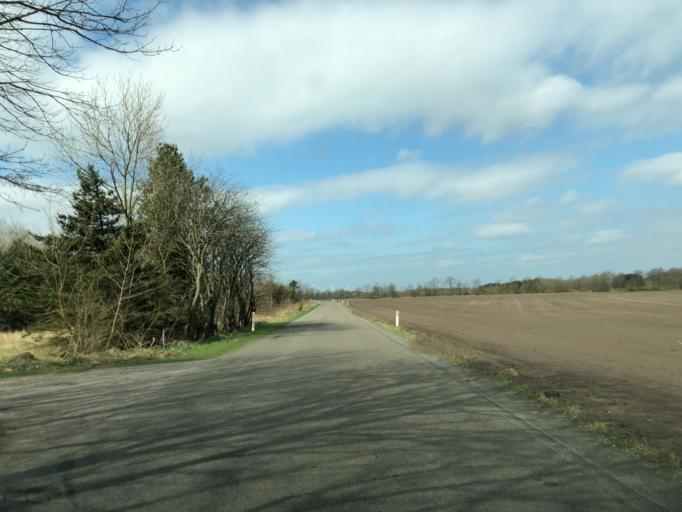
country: DK
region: South Denmark
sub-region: Vejle Kommune
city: Give
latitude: 55.9131
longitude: 9.2447
